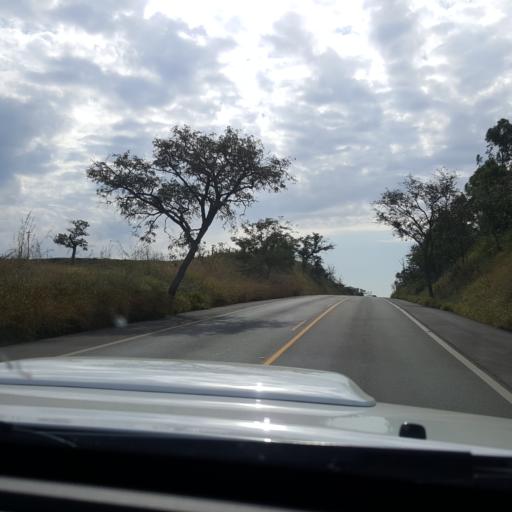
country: BR
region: Sao Paulo
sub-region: Itaporanga
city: Itaporanga
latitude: -23.7512
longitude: -49.4529
